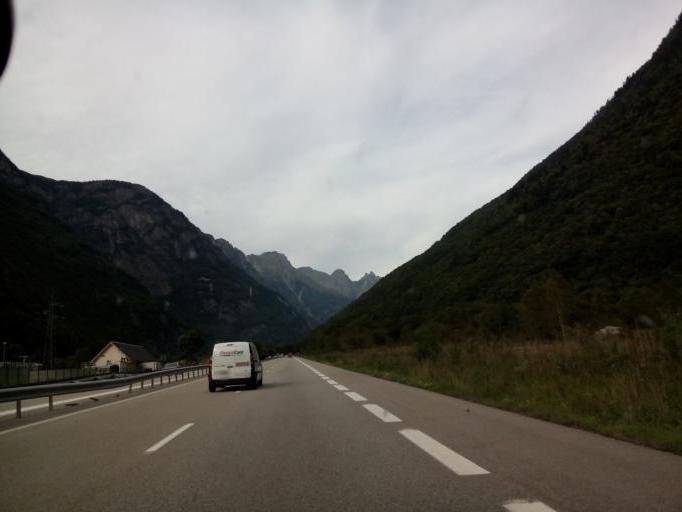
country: FR
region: Rhone-Alpes
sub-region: Departement de l'Isere
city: Vaulnaveys-le-Bas
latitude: 45.0573
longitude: 5.8608
